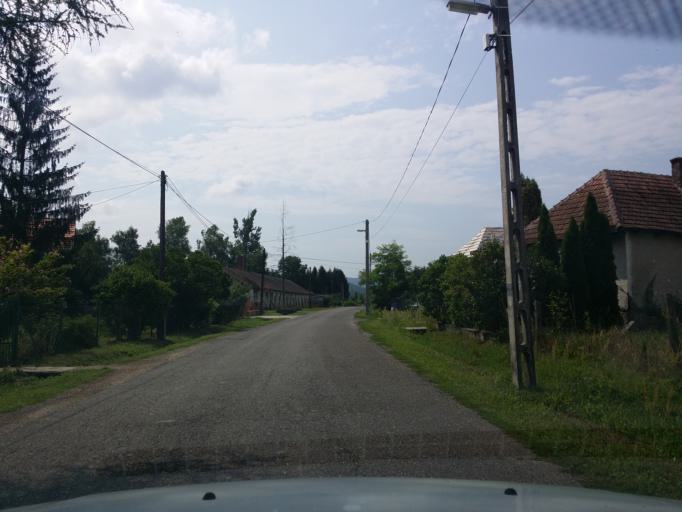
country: HU
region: Borsod-Abauj-Zemplen
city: Sarospatak
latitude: 48.4494
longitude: 21.5292
